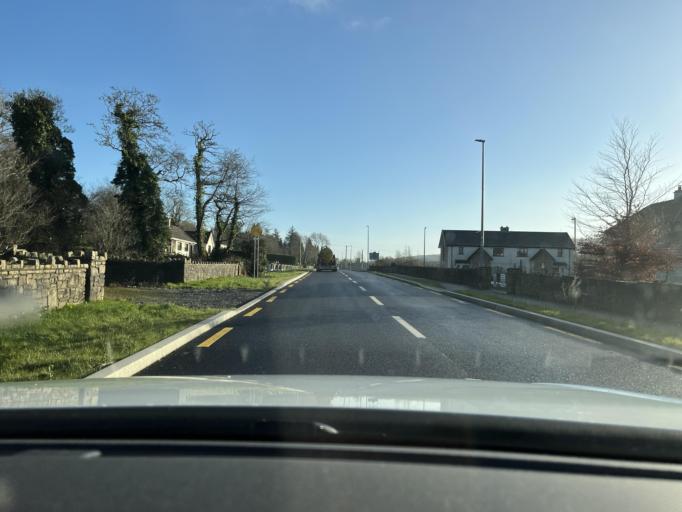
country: IE
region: Connaught
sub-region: County Leitrim
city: Manorhamilton
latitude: 54.1734
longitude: -8.1505
